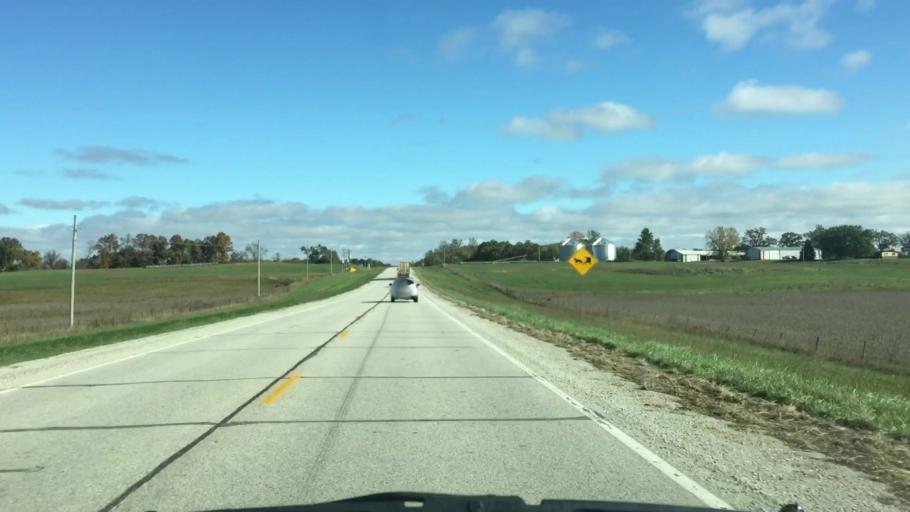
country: US
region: Iowa
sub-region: Decatur County
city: Leon
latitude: 40.6450
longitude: -93.8051
